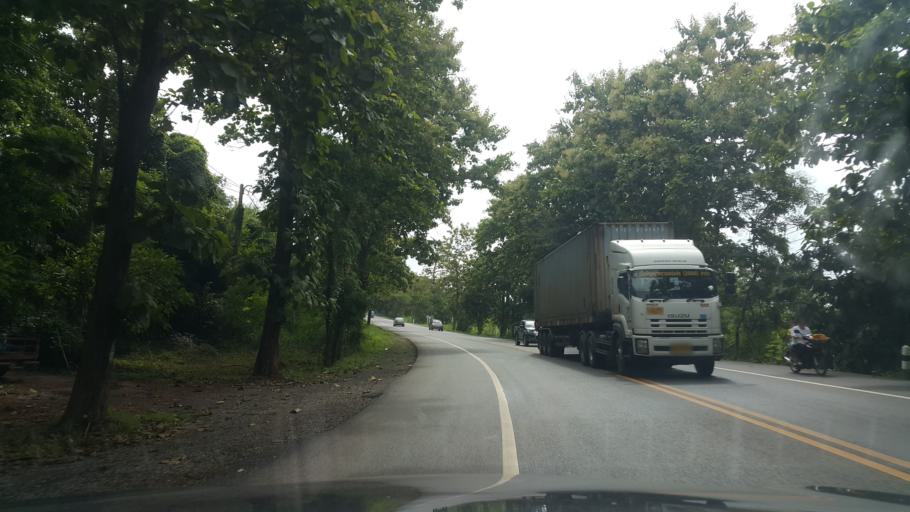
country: TH
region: Uttaradit
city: Lap Lae
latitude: 17.5968
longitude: 100.0283
